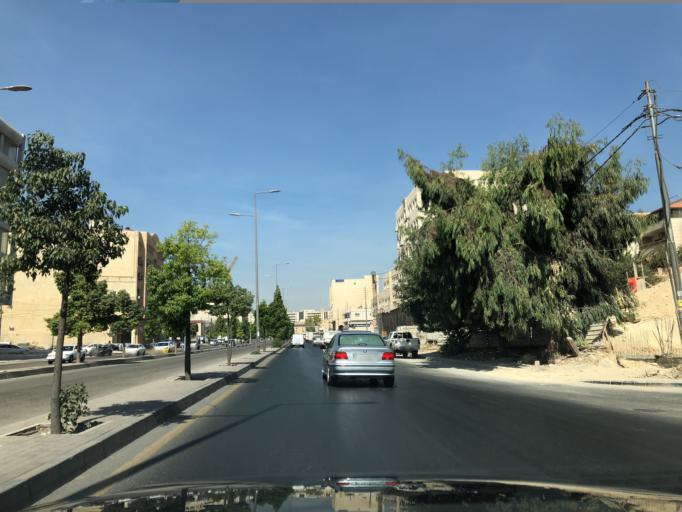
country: JO
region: Amman
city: Al Jubayhah
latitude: 32.0206
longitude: 35.8628
